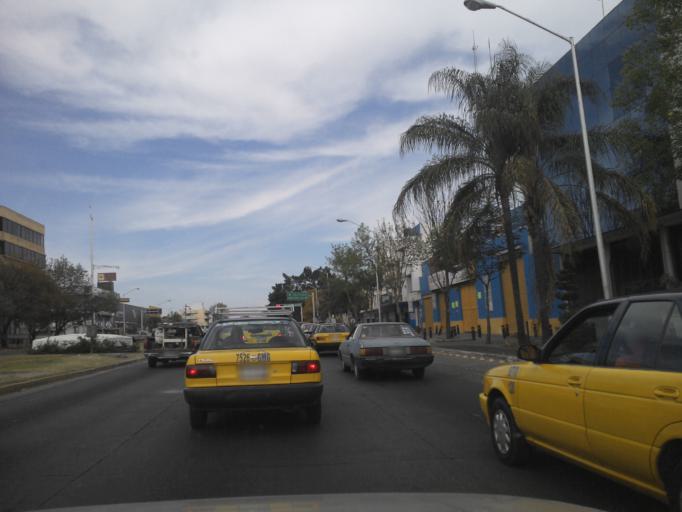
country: MX
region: Jalisco
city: Guadalajara
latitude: 20.6648
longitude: -103.3559
